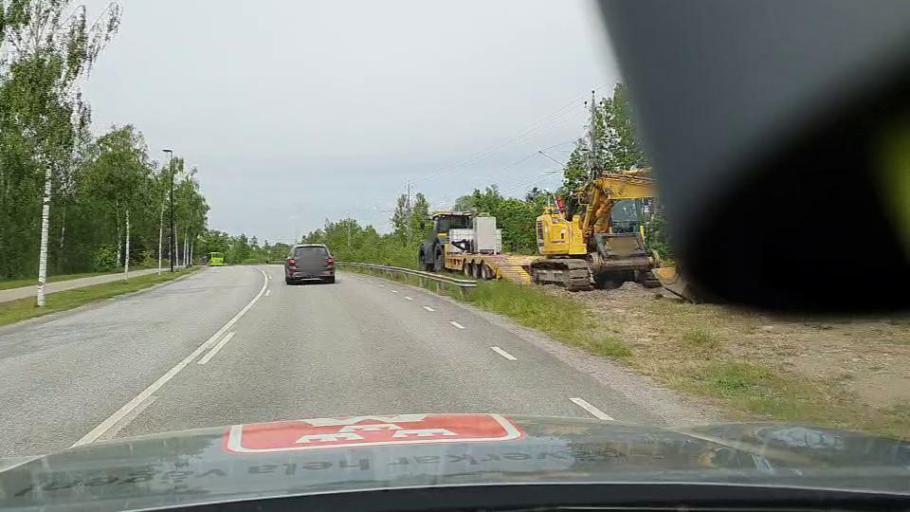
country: SE
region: Soedermanland
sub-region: Flens Kommun
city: Flen
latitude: 59.0637
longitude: 16.5935
